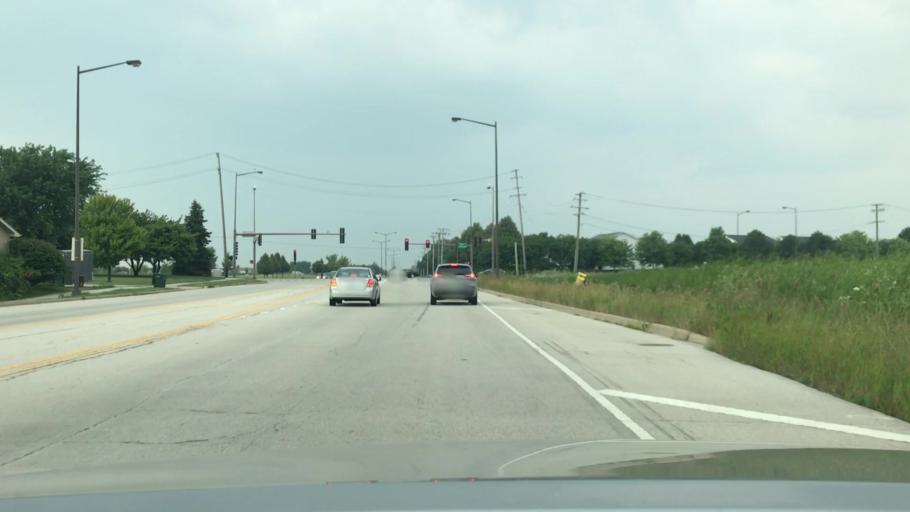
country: US
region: Illinois
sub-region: Kendall County
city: Boulder Hill
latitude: 41.6962
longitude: -88.2538
